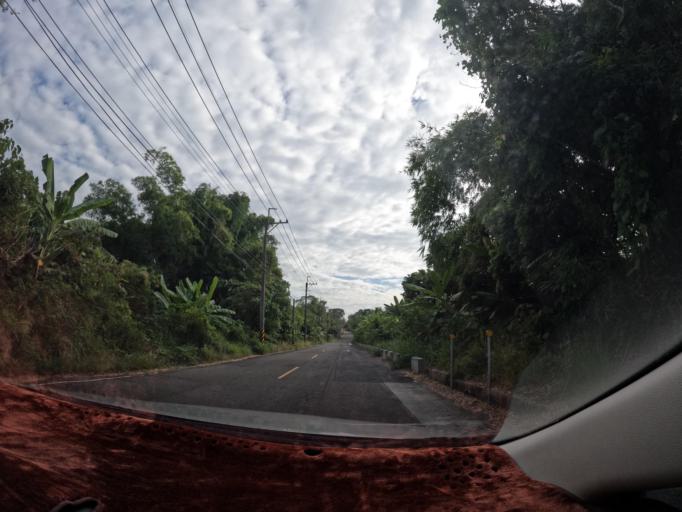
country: TW
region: Taiwan
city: Yujing
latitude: 23.0147
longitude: 120.4167
